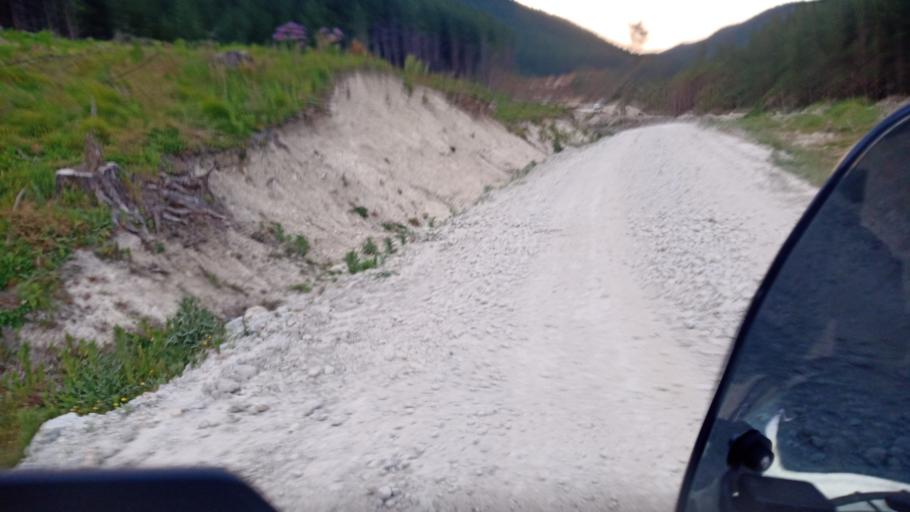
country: NZ
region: Gisborne
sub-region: Gisborne District
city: Gisborne
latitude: -38.4657
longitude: 177.9602
